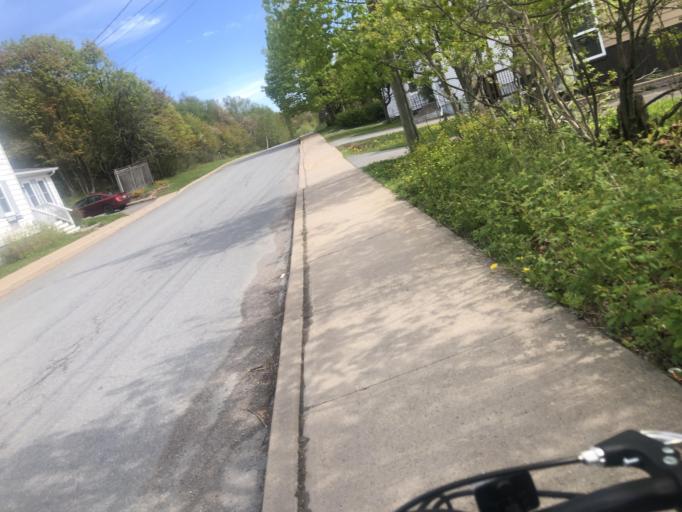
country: CA
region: New Brunswick
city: Saint John
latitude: 45.2840
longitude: -66.0833
